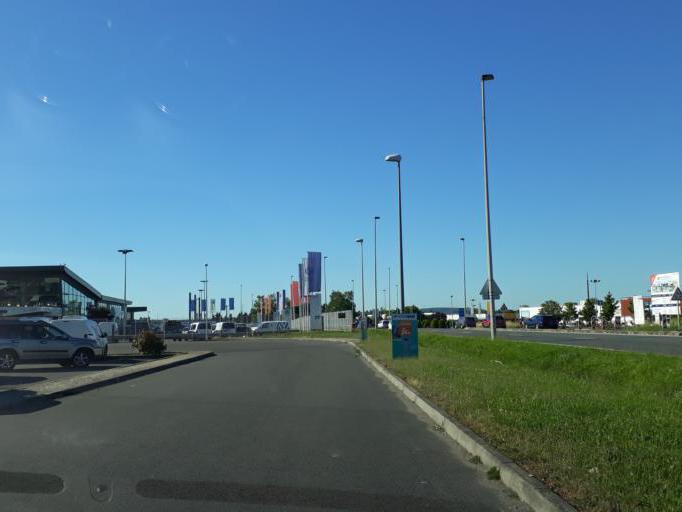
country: FR
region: Centre
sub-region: Departement du Cher
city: Saint-Doulchard
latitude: 47.1166
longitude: 2.3750
